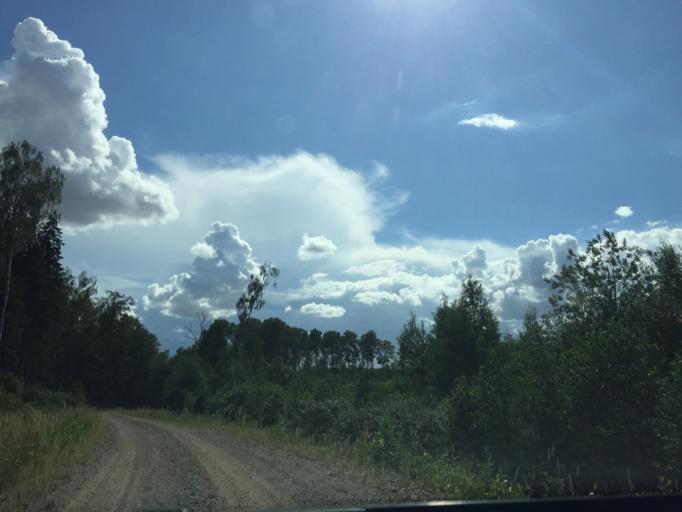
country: LT
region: Siauliu apskritis
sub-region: Joniskis
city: Joniskis
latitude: 56.3507
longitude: 23.5809
